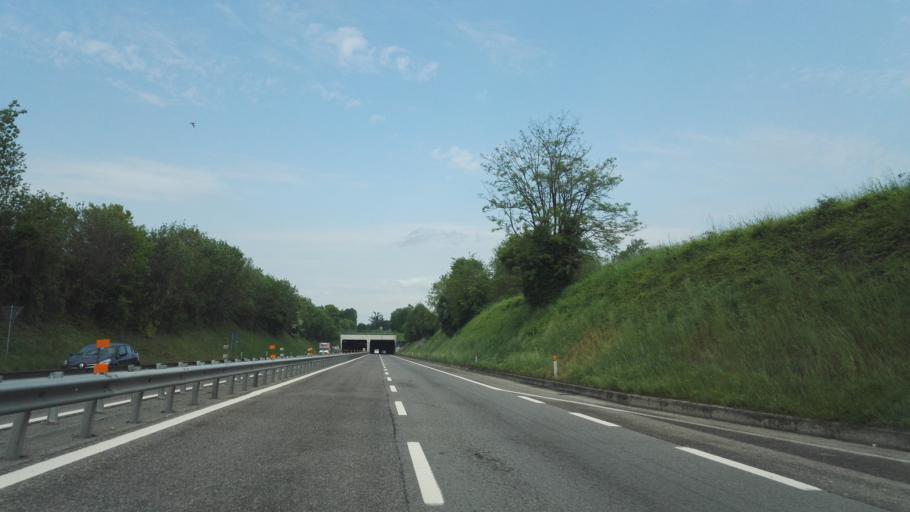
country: IT
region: Lombardy
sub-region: Provincia di Monza e Brianza
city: Lentate sul Seveso
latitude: 45.6715
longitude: 9.1154
